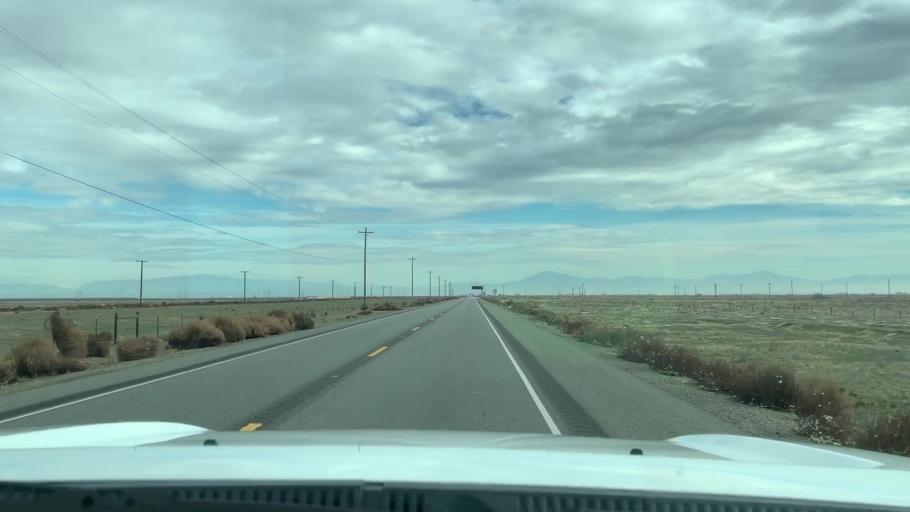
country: US
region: California
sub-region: Kern County
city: Rosedale
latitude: 35.2676
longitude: -119.2958
